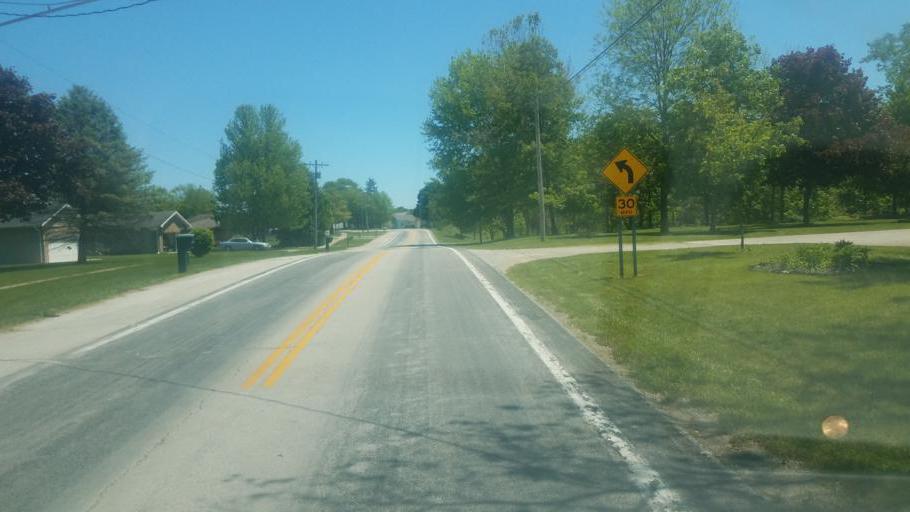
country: US
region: Ohio
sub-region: Darke County
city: Versailles
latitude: 40.2304
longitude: -84.4984
